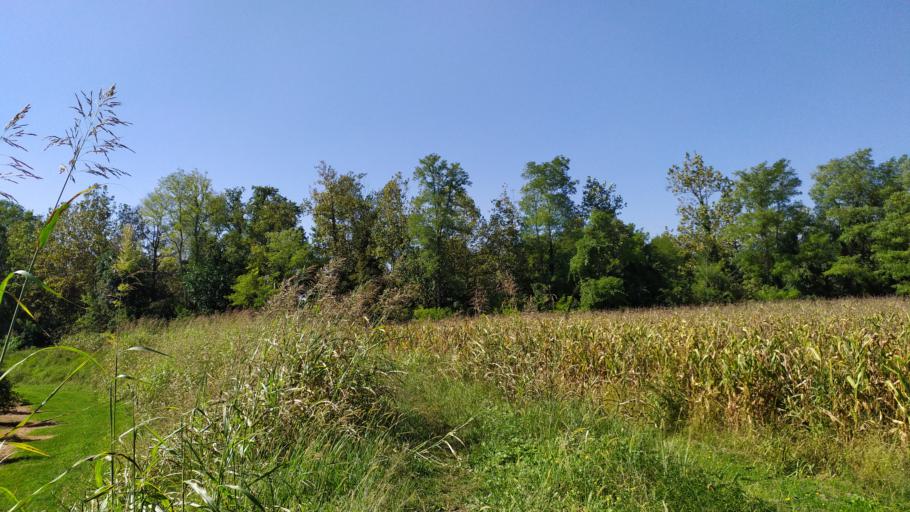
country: IT
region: Friuli Venezia Giulia
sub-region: Provincia di Pordenone
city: Cavolano-Schiavoi
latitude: 45.9392
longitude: 12.4803
